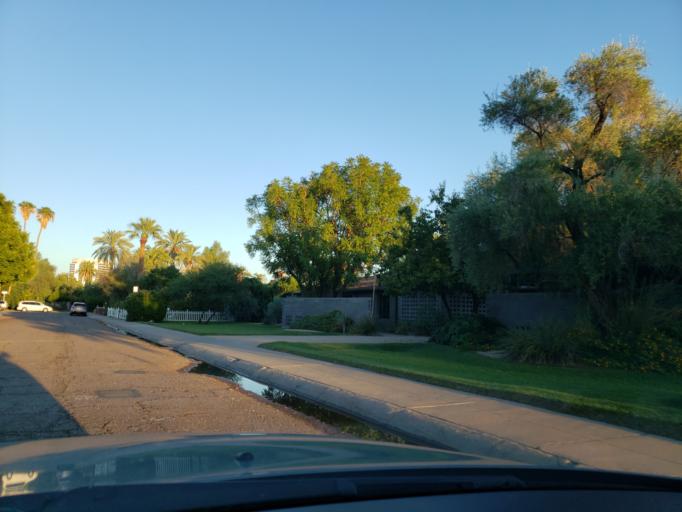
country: US
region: Arizona
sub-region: Maricopa County
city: Phoenix
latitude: 33.4794
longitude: -112.0852
